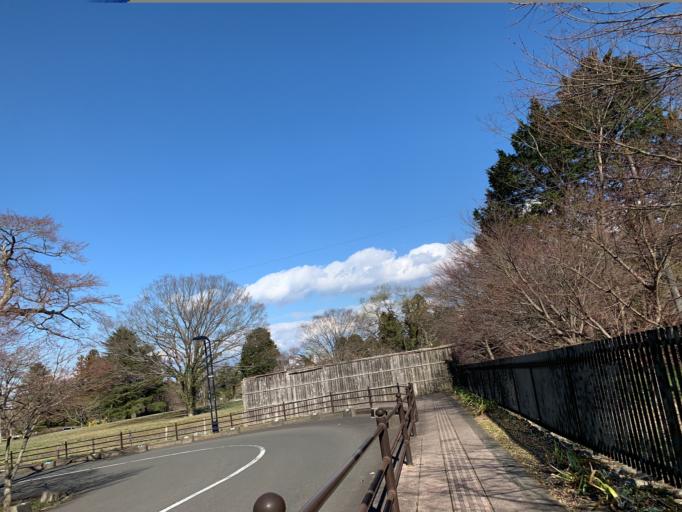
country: JP
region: Miyagi
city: Sendai
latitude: 38.2562
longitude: 140.8538
